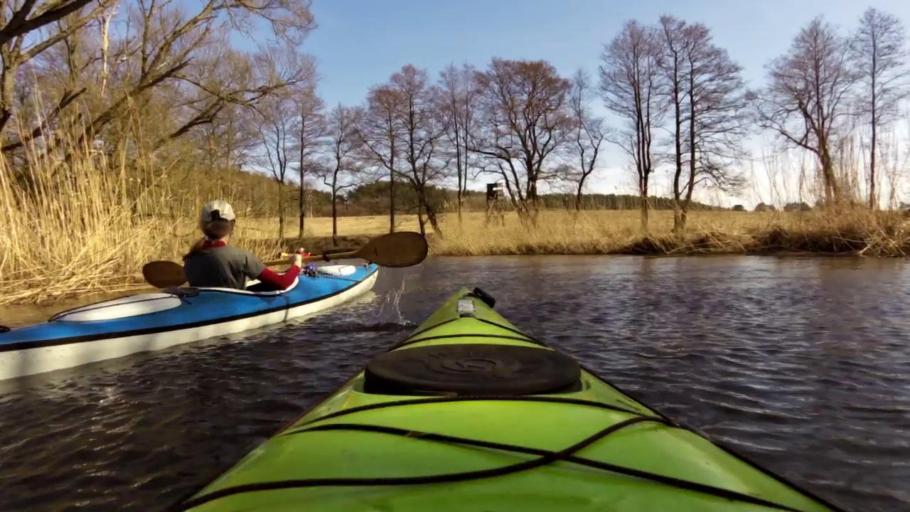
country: PL
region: West Pomeranian Voivodeship
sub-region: Powiat lobeski
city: Lobez
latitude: 53.6693
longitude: 15.5657
